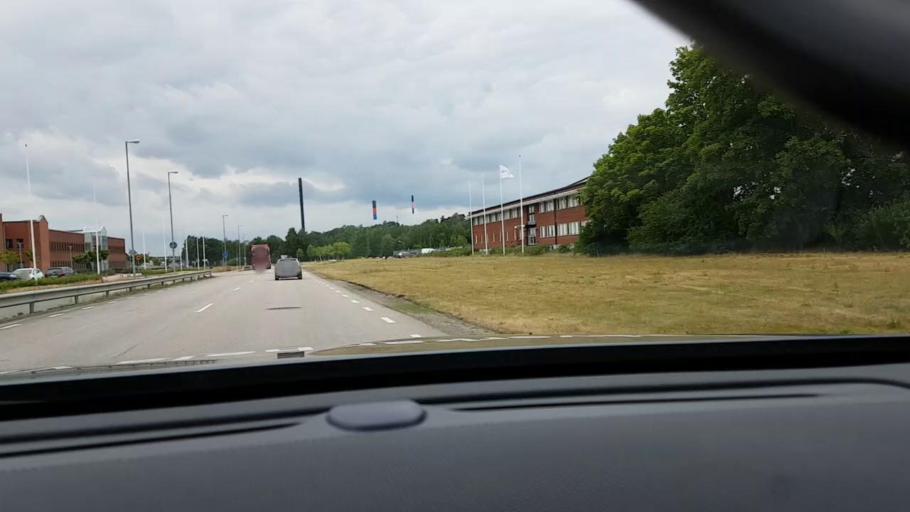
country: SE
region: Skane
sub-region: Hassleholms Kommun
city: Hassleholm
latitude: 56.1584
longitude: 13.8069
